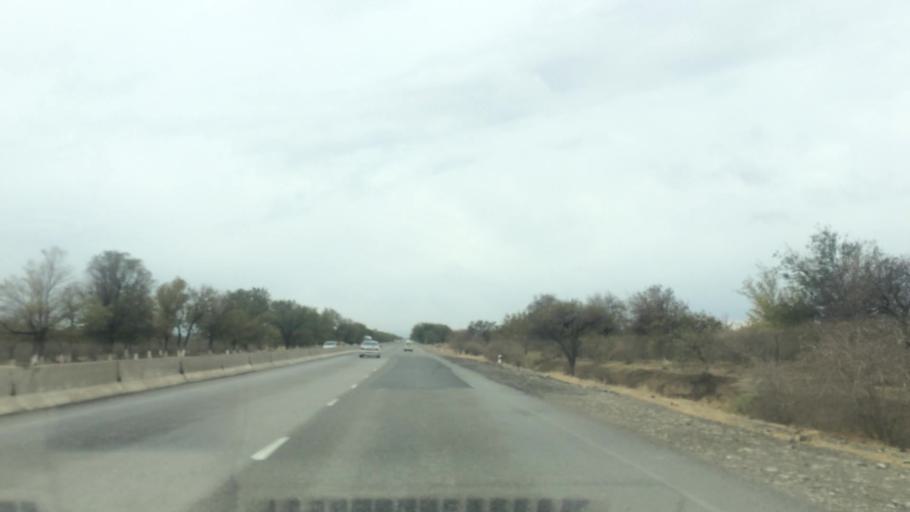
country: UZ
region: Samarqand
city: Bulung'ur
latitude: 39.8161
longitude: 67.3788
